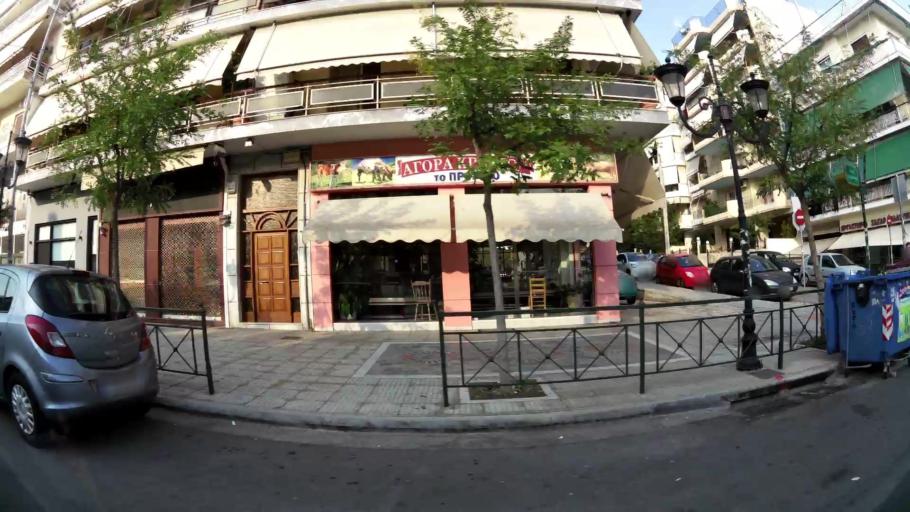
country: GR
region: Attica
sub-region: Nomarchia Athinas
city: Petroupolis
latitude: 38.0437
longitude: 23.6812
